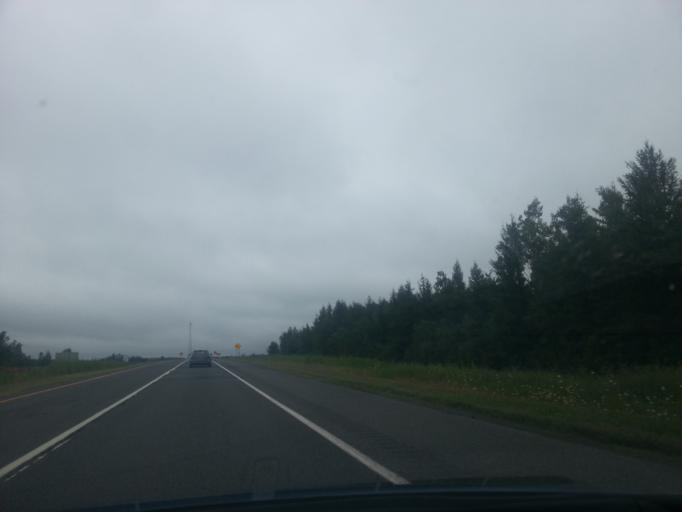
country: CA
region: Quebec
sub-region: Mauricie
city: Daveluyville
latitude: 46.2311
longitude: -72.0591
